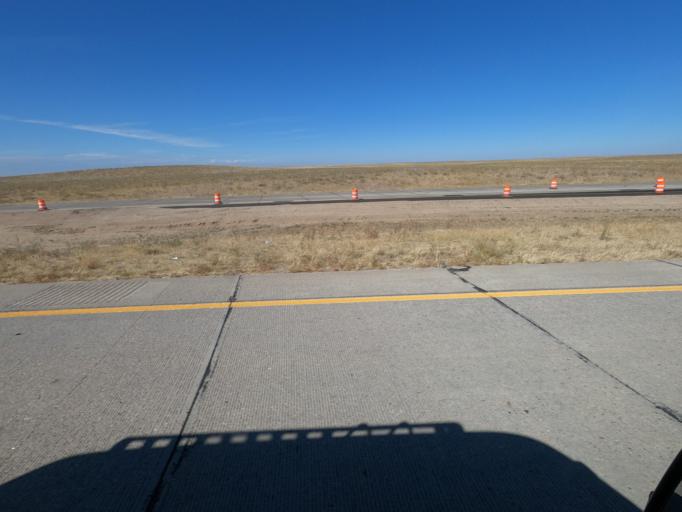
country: US
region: Colorado
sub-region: Weld County
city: Keenesburg
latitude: 40.2030
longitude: -104.2515
